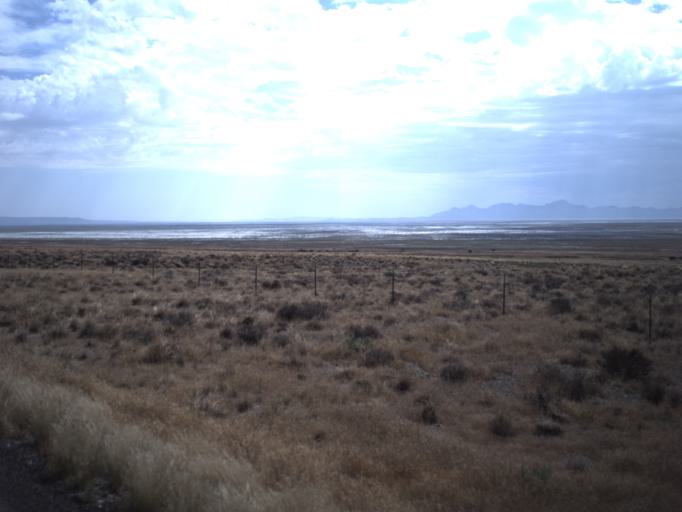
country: US
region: Utah
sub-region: Tooele County
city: Wendover
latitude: 41.4387
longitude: -113.7252
